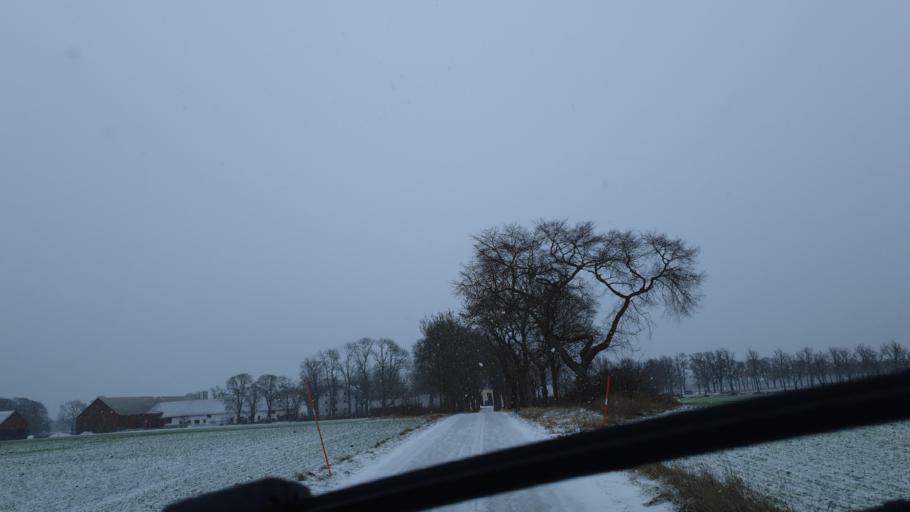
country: SE
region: Gotland
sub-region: Gotland
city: Visby
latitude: 57.5183
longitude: 18.4560
